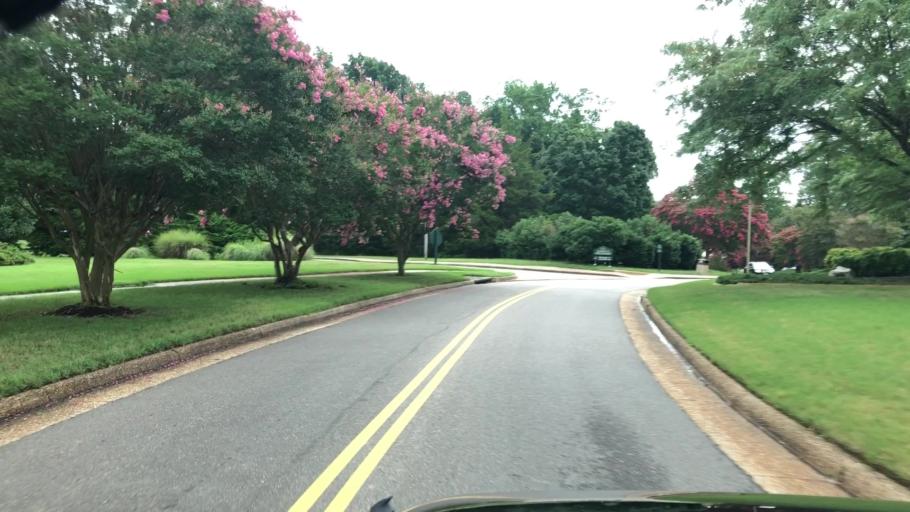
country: US
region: Virginia
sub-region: City of Williamsburg
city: Williamsburg
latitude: 37.2251
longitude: -76.6650
